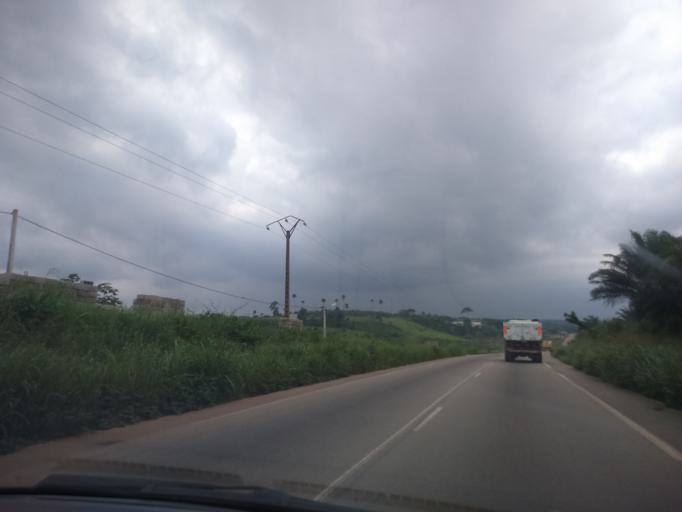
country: CI
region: Lagunes
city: Anyama
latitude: 5.5019
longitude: -4.0651
